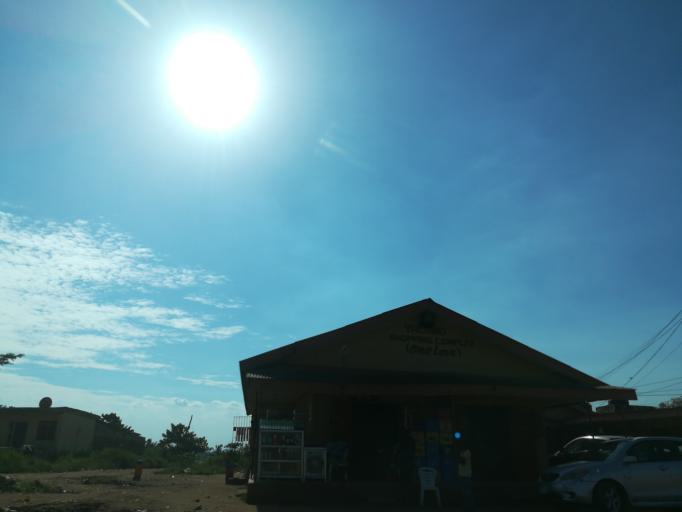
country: NG
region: Lagos
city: Ikorodu
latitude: 6.5811
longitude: 3.5226
